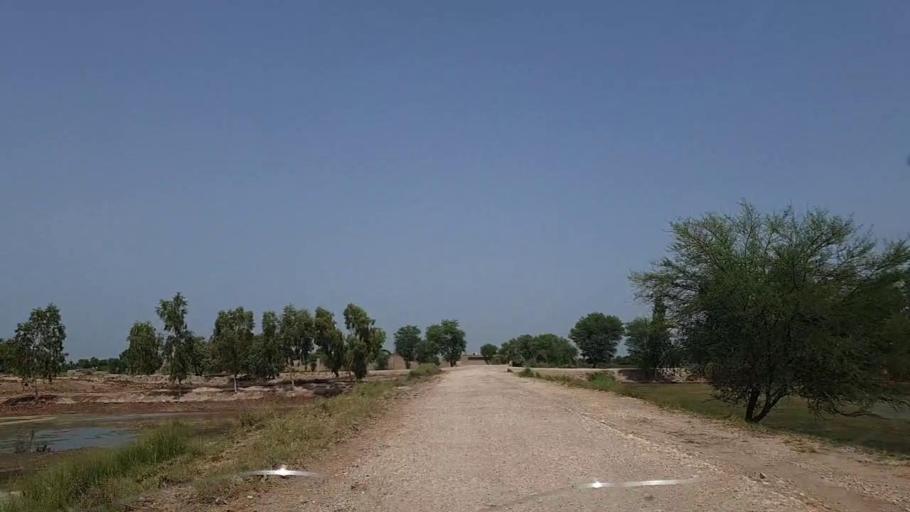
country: PK
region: Sindh
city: Tharu Shah
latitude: 27.0145
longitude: 68.1442
